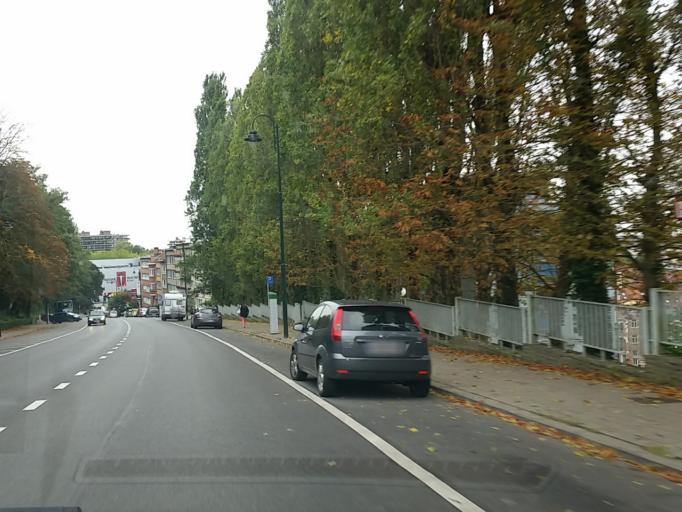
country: BE
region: Flanders
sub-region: Provincie Vlaams-Brabant
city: Drogenbos
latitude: 50.8125
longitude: 4.3286
